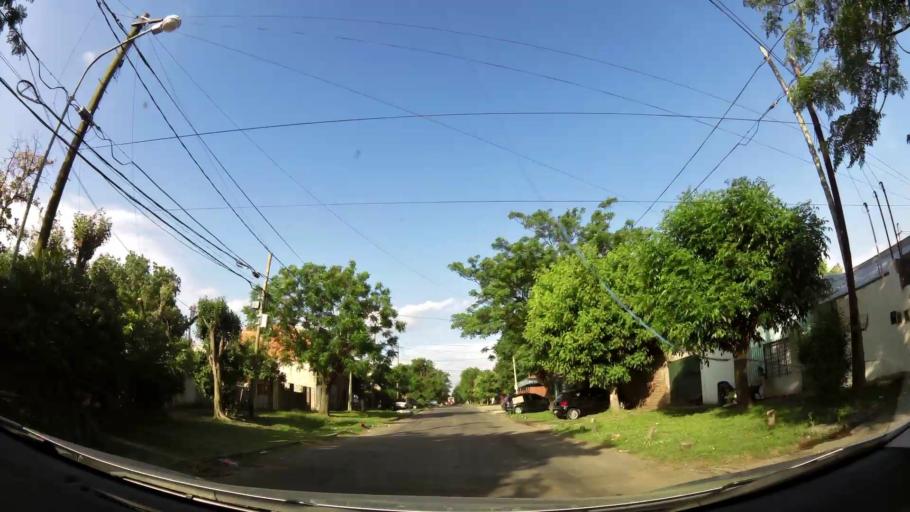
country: AR
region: Buenos Aires
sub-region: Partido de Tigre
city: Tigre
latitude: -34.4691
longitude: -58.6617
